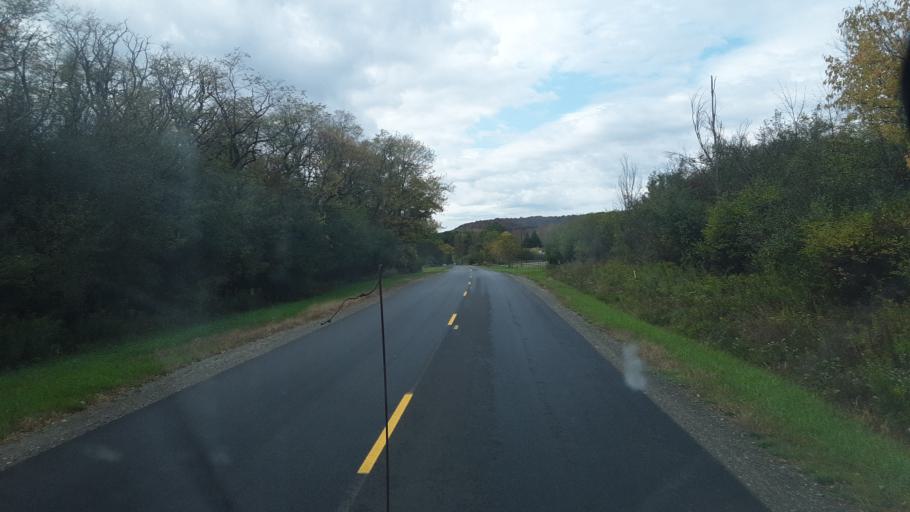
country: US
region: New York
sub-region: Allegany County
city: Alfred
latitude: 42.3696
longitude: -77.8026
